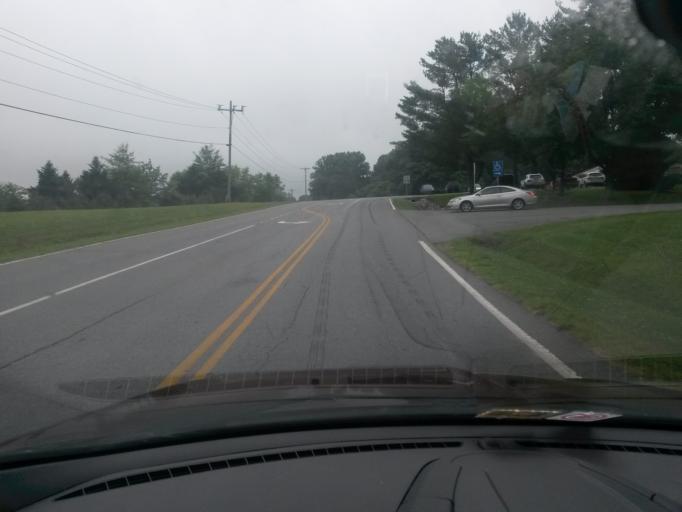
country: US
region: Virginia
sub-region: City of Bedford
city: Bedford
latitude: 37.3195
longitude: -79.4838
